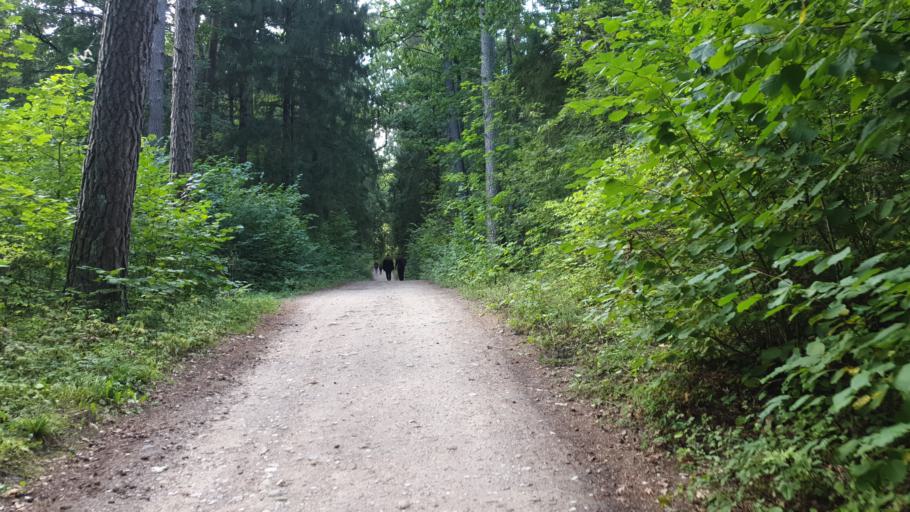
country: LT
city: Trakai
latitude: 54.6470
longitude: 24.9718
